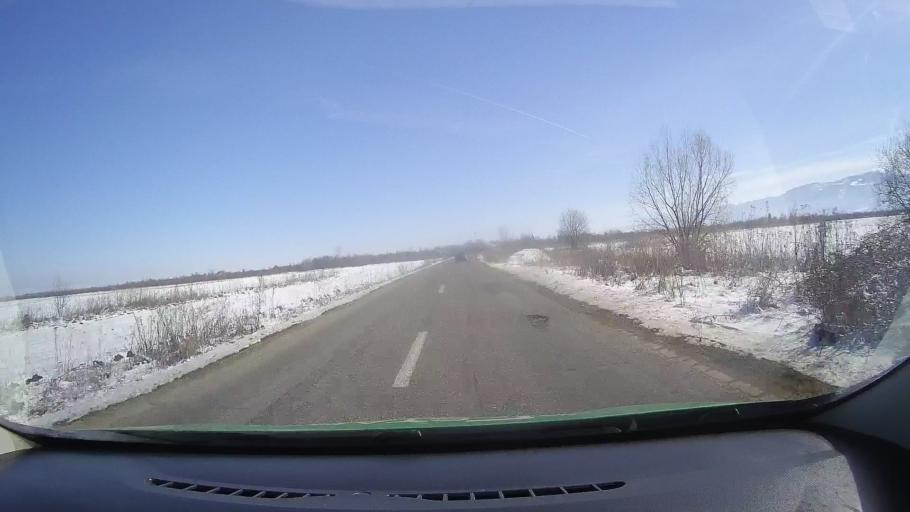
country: RO
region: Brasov
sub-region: Comuna Recea
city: Recea
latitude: 45.7278
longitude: 24.8918
